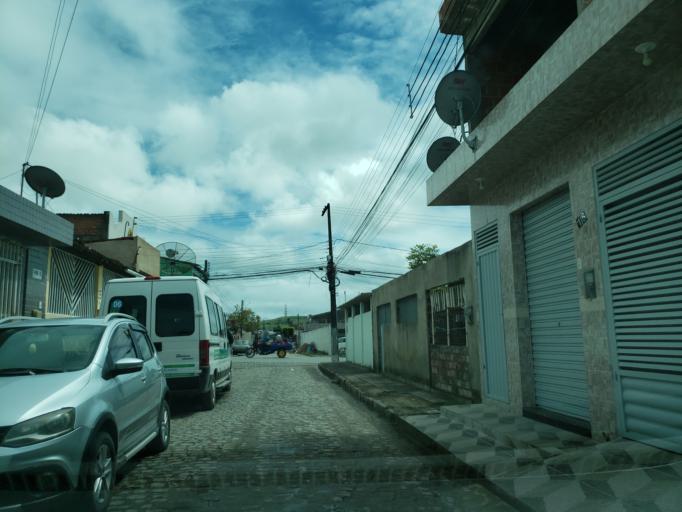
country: BR
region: Alagoas
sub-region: Uniao Dos Palmares
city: Uniao dos Palmares
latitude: -9.1584
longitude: -36.0255
